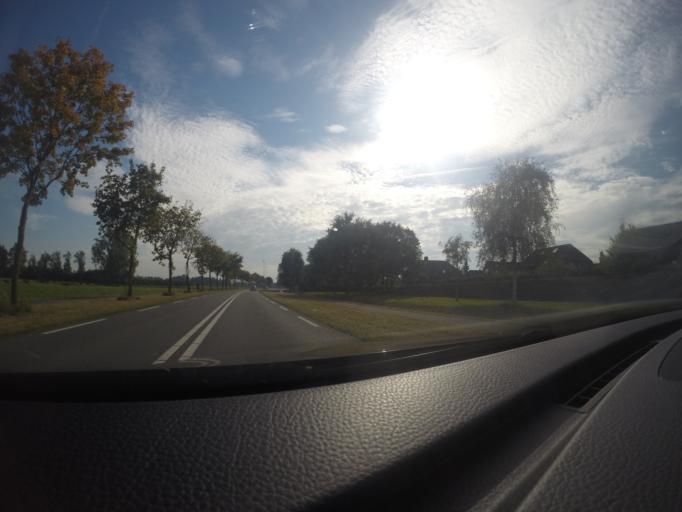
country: NL
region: Gelderland
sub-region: Gemeente Doetinchem
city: Doetinchem
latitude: 51.9611
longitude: 6.2198
